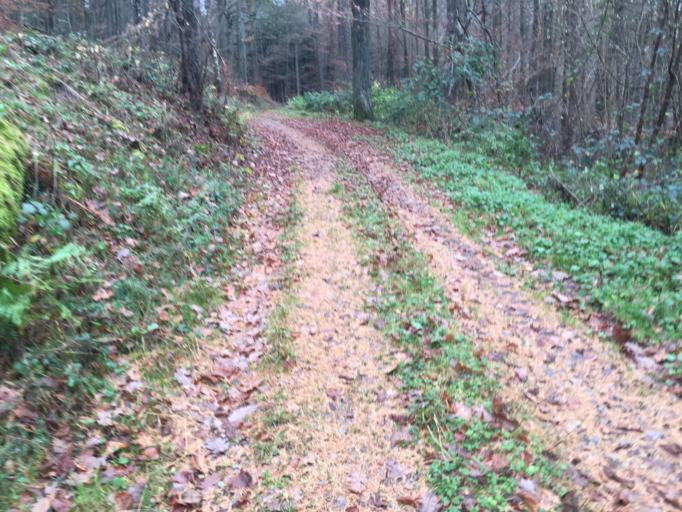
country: DE
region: Baden-Wuerttemberg
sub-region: Karlsruhe Region
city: Eberbach
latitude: 49.4684
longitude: 9.0036
